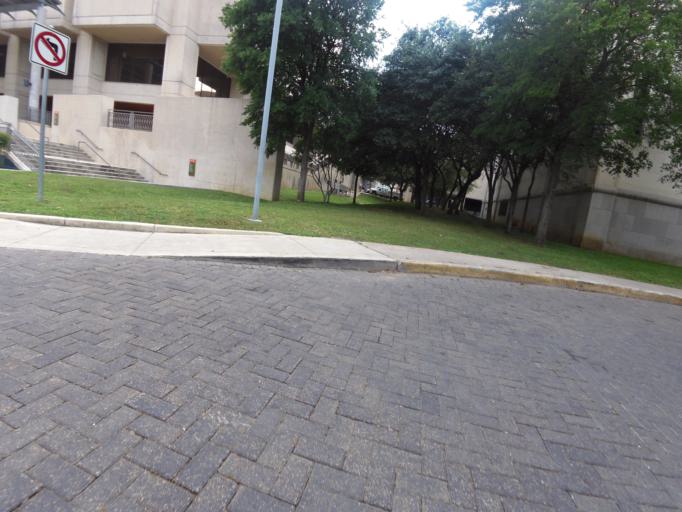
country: US
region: Texas
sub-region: Bexar County
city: Shavano Park
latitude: 29.5851
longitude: -98.6174
